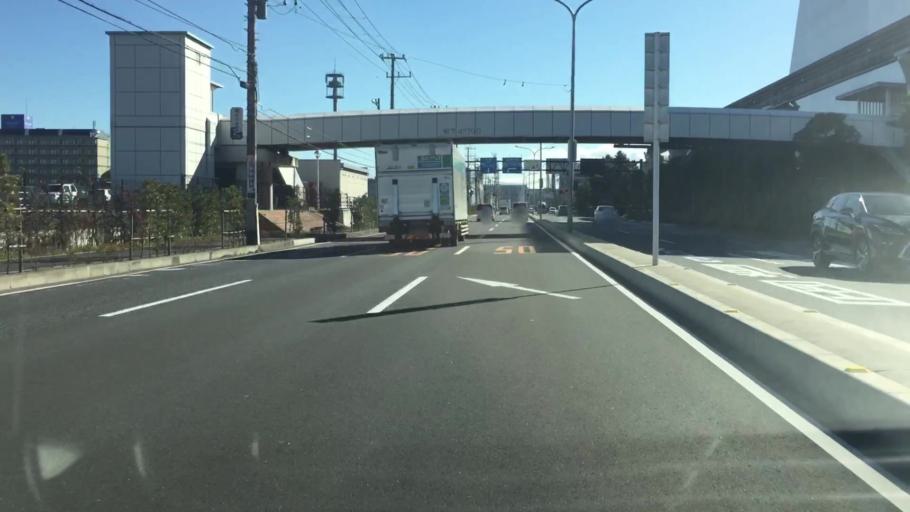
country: JP
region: Tokyo
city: Urayasu
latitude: 35.6337
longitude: 139.8890
